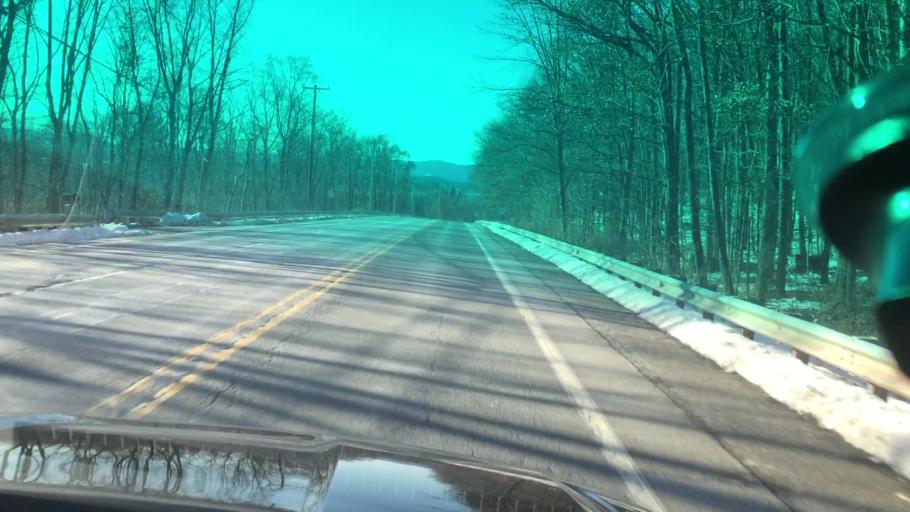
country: US
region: Pennsylvania
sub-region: Luzerne County
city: Harleigh
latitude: 41.0184
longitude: -75.9539
